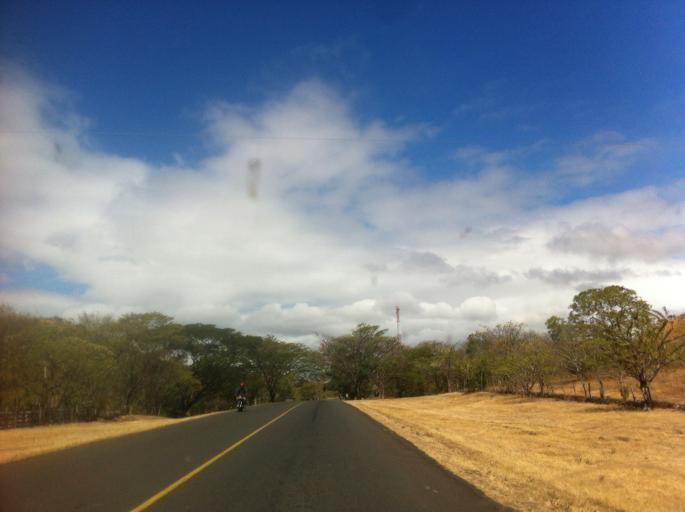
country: NI
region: Chontales
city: Acoyapa
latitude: 12.0168
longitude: -85.2488
